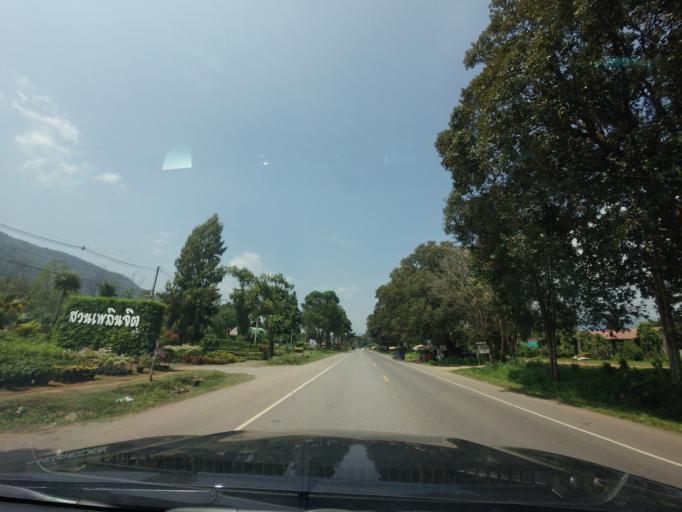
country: TH
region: Loei
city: Phu Ruea
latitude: 17.4593
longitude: 101.4050
